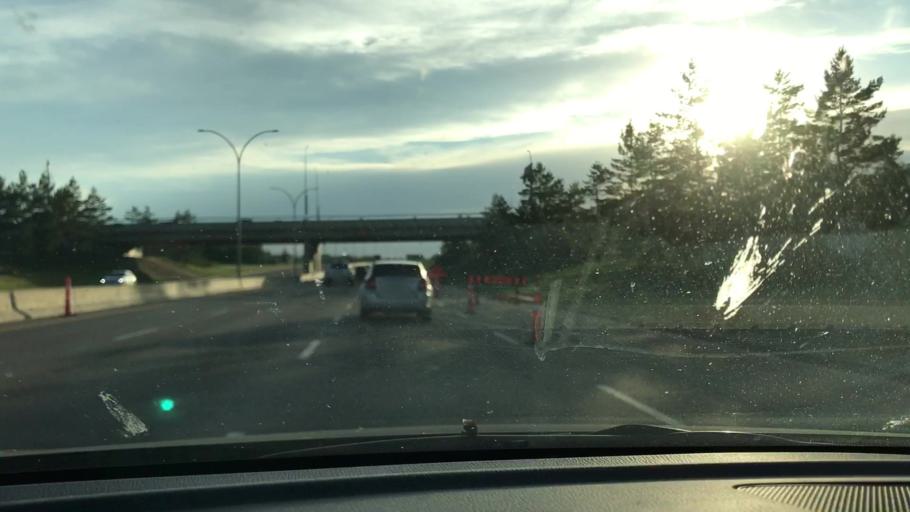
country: CA
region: Alberta
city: Edmonton
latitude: 53.4805
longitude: -113.4936
